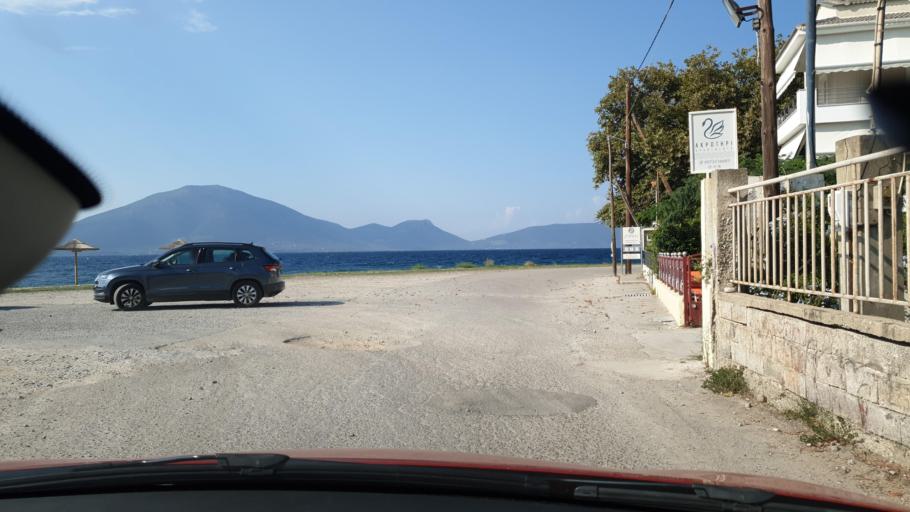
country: GR
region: Central Greece
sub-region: Nomos Evvoias
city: Oreoi
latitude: 38.9359
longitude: 23.0346
